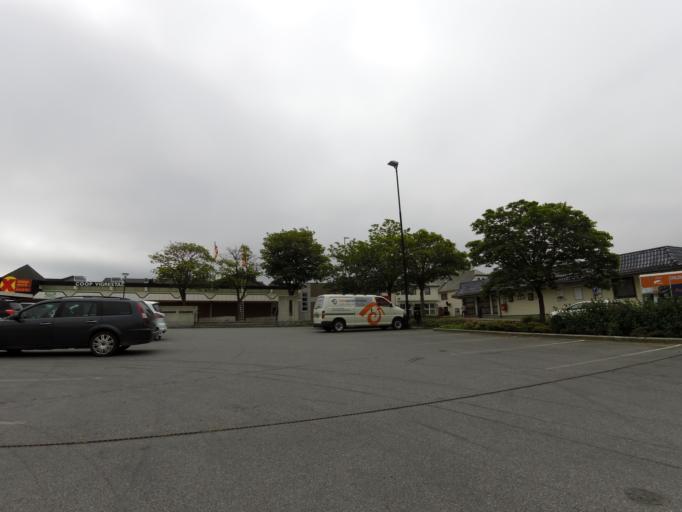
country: NO
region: Rogaland
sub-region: Ha
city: Vigrestad
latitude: 58.5710
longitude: 5.6897
